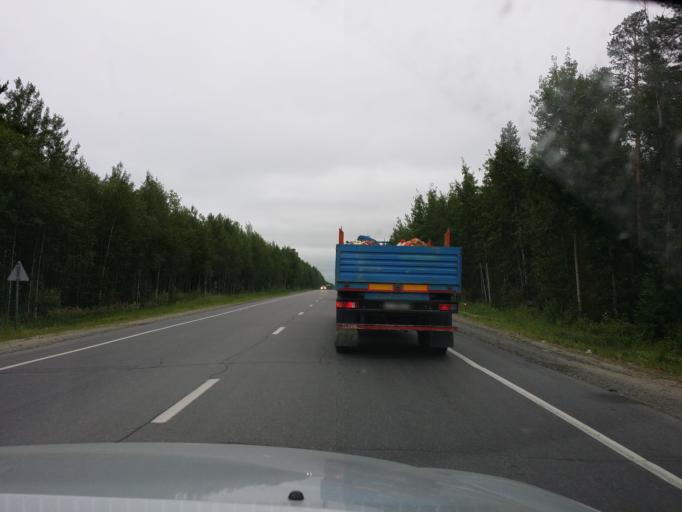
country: RU
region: Khanty-Mansiyskiy Avtonomnyy Okrug
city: Megion
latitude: 61.0557
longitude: 76.3044
